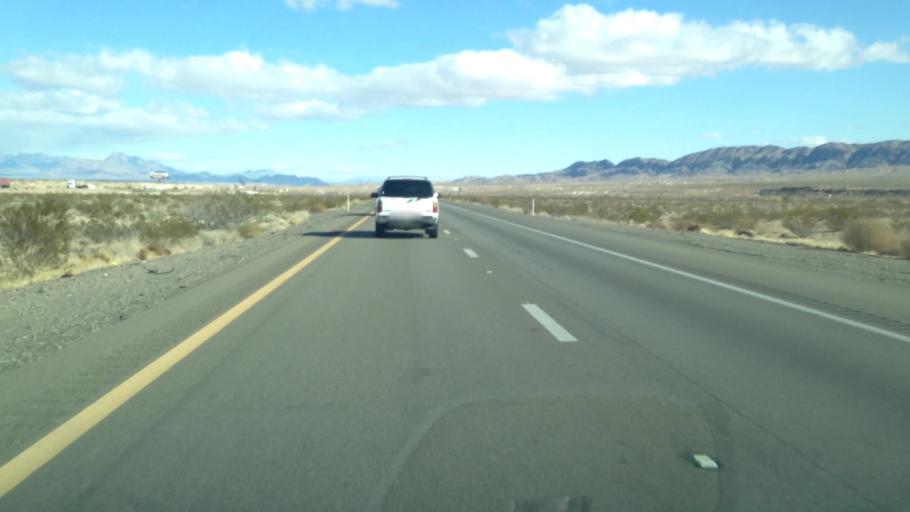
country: US
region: Nevada
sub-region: Clark County
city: Moapa Town
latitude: 36.5467
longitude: -114.7039
